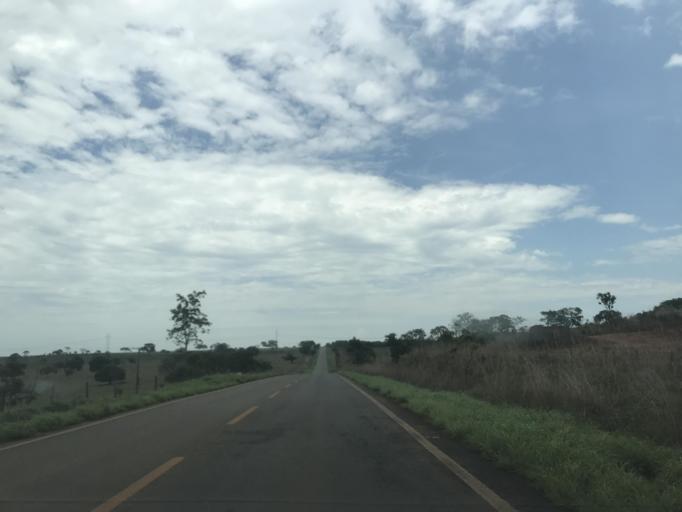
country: BR
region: Goias
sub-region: Luziania
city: Luziania
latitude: -16.2776
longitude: -47.9946
